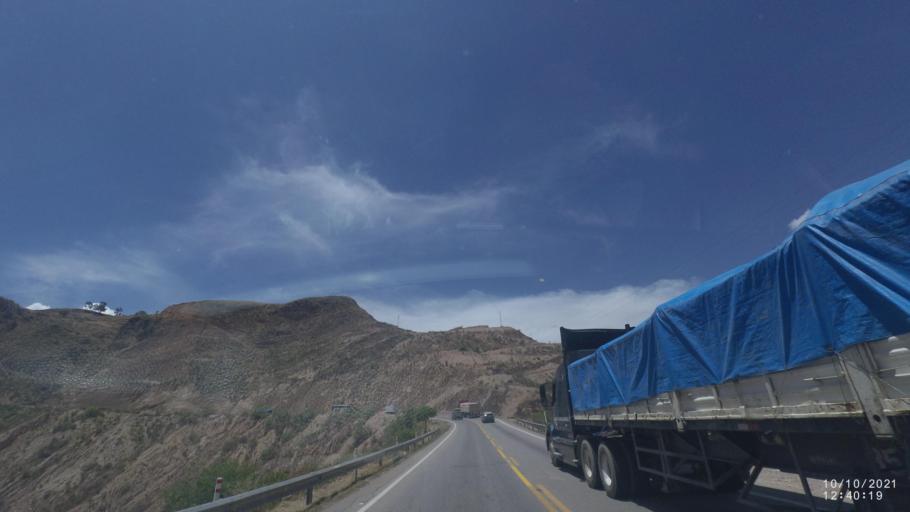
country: BO
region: Cochabamba
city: Irpa Irpa
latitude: -17.6414
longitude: -66.3899
